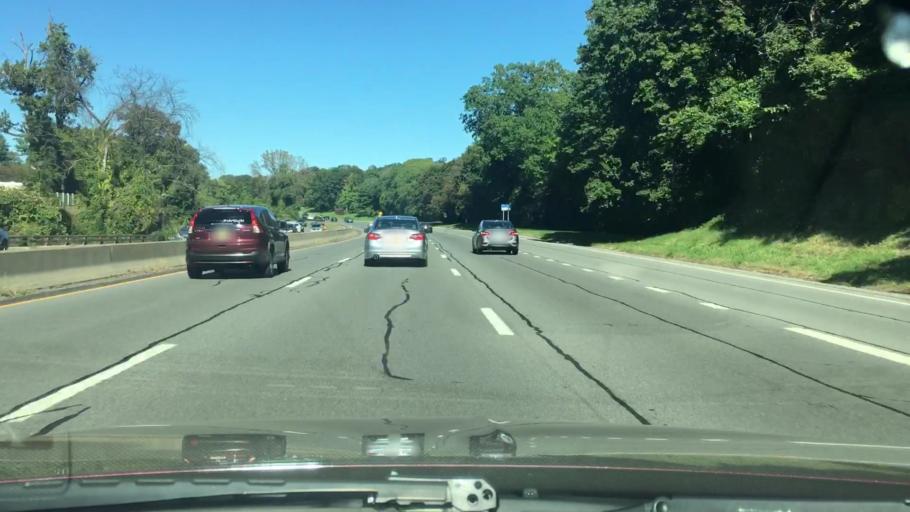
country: US
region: New York
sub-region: Westchester County
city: Tuckahoe
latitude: 40.9546
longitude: -73.8523
